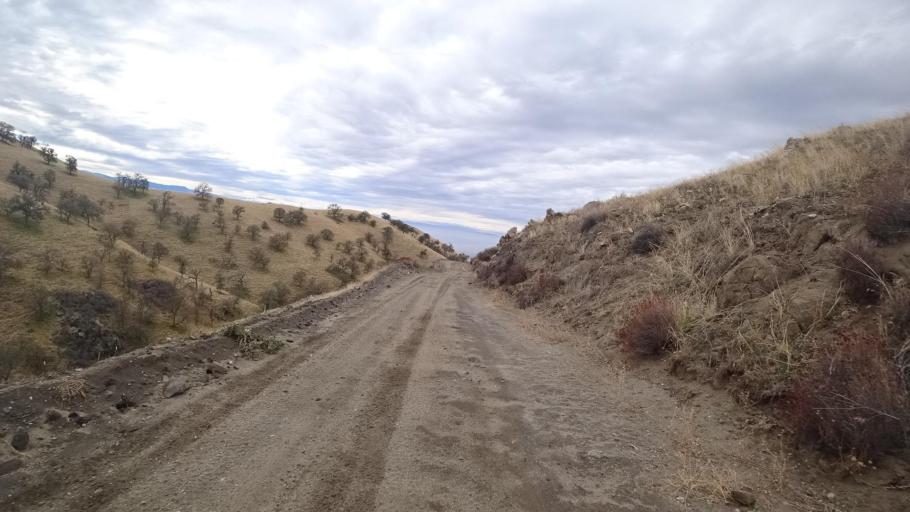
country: US
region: California
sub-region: Kern County
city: Arvin
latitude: 35.1267
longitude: -118.7569
